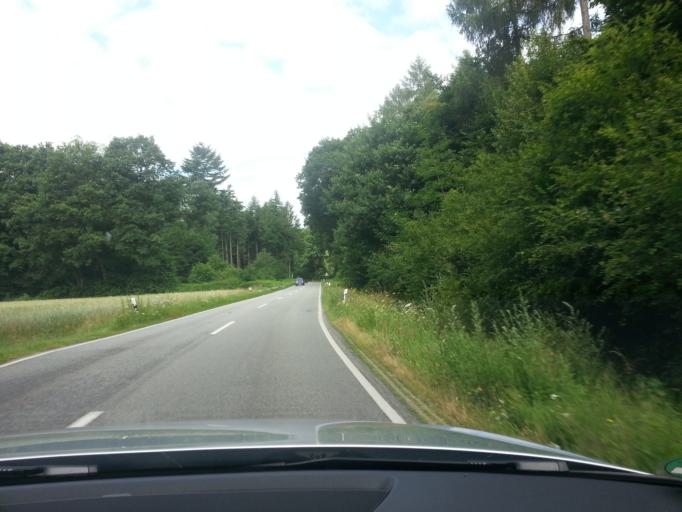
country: DE
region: Saarland
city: Schmelz
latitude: 49.4739
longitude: 6.8156
